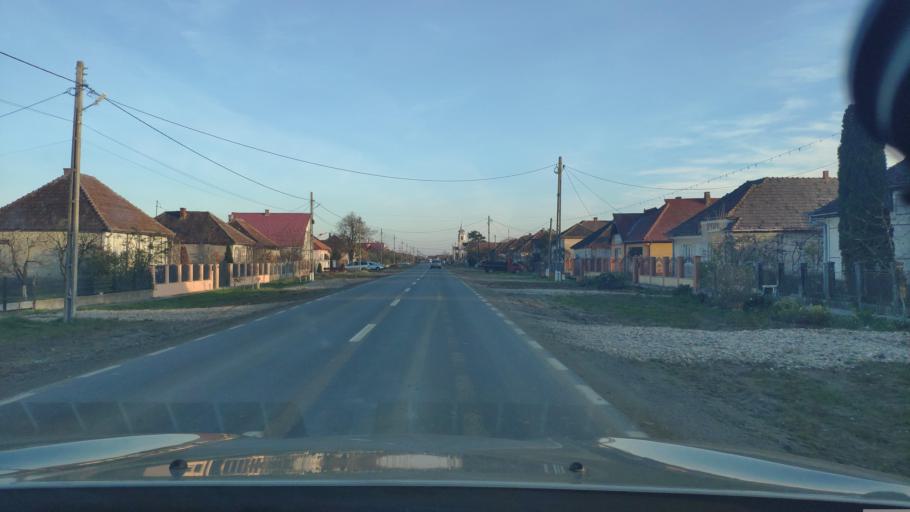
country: RO
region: Satu Mare
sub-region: Comuna Mediesu Aurit
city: Potau
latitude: 47.7782
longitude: 23.0903
